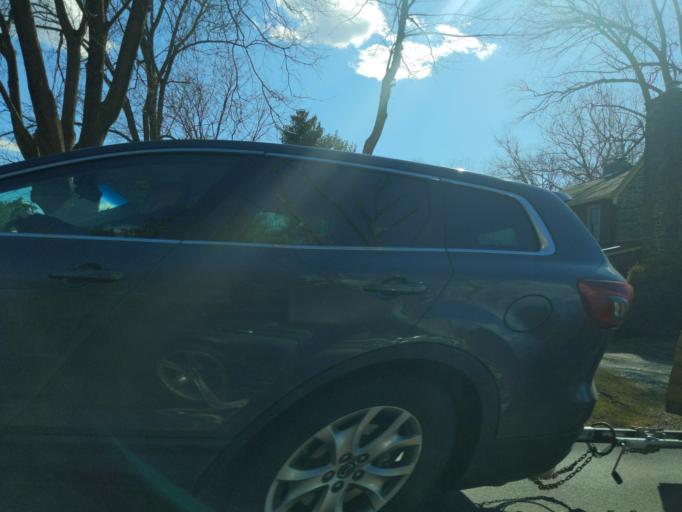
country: US
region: Pennsylvania
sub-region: Montgomery County
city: Red Hill
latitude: 40.3865
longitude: -75.4670
